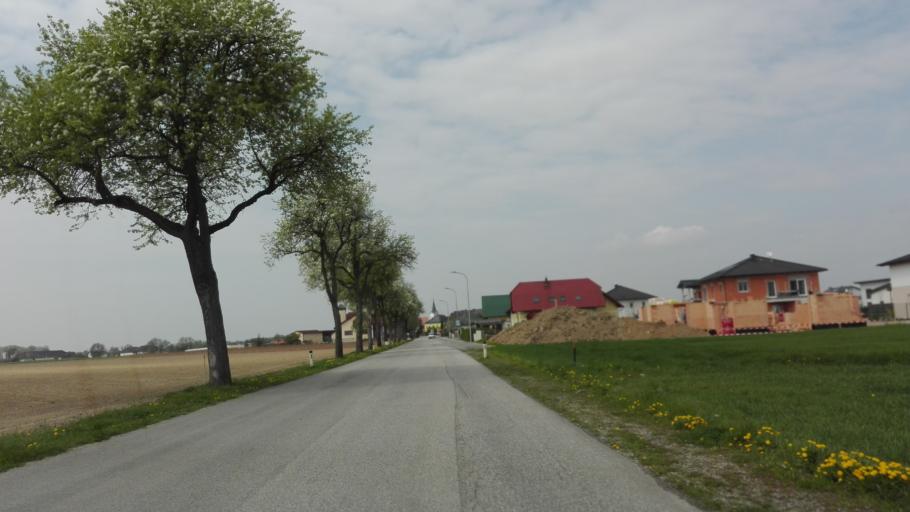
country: AT
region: Upper Austria
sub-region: Politischer Bezirk Perg
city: Perg
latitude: 48.2216
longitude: 14.6192
